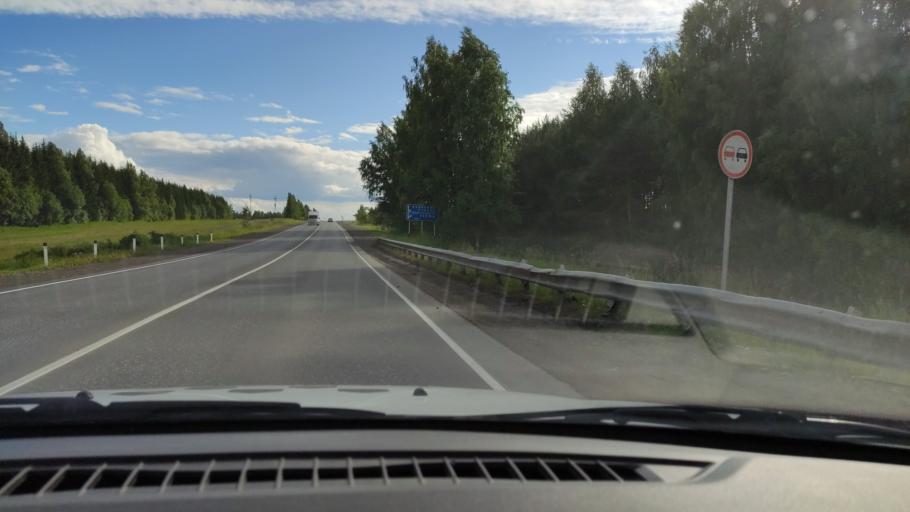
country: RU
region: Perm
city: Kungur
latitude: 57.4084
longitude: 56.9022
